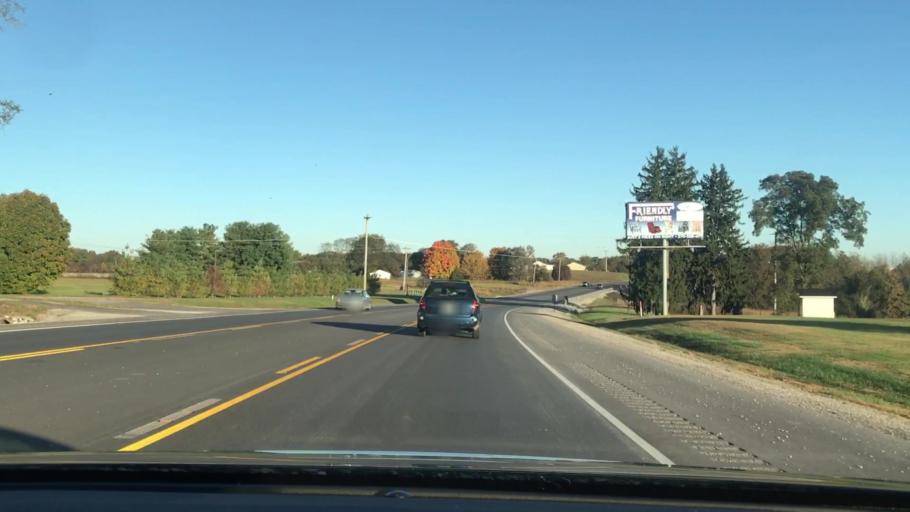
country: US
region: Kentucky
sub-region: Simpson County
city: Franklin
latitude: 36.6792
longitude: -86.5653
